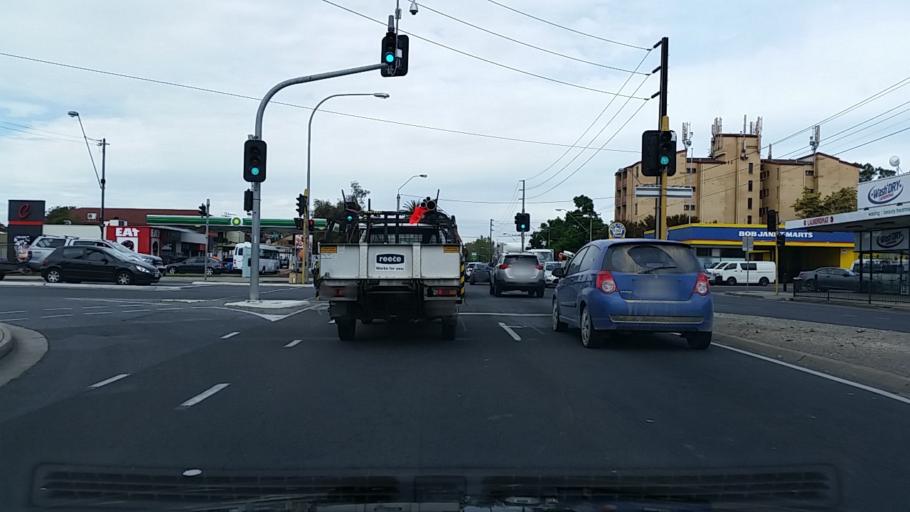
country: AU
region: South Australia
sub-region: City of West Torrens
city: Thebarton
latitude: -34.9247
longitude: 138.5487
